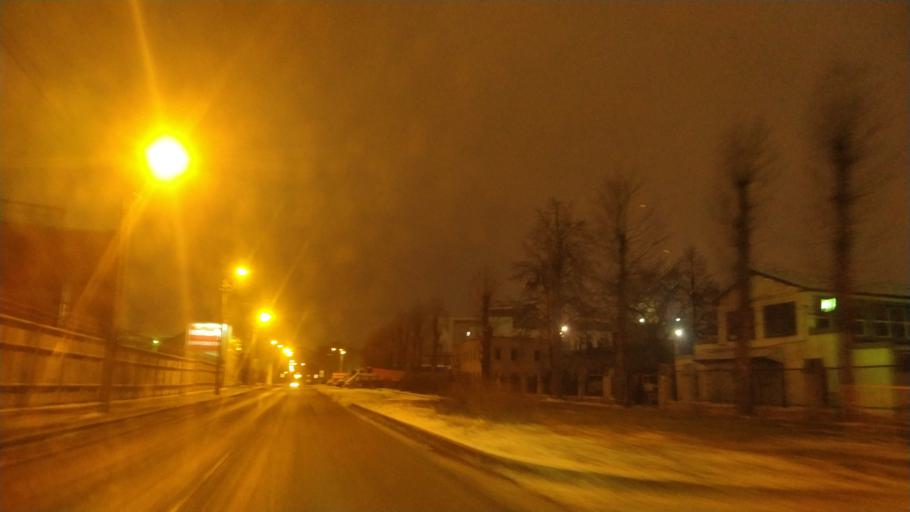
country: RU
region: St.-Petersburg
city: Kupchino
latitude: 59.8822
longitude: 30.3332
